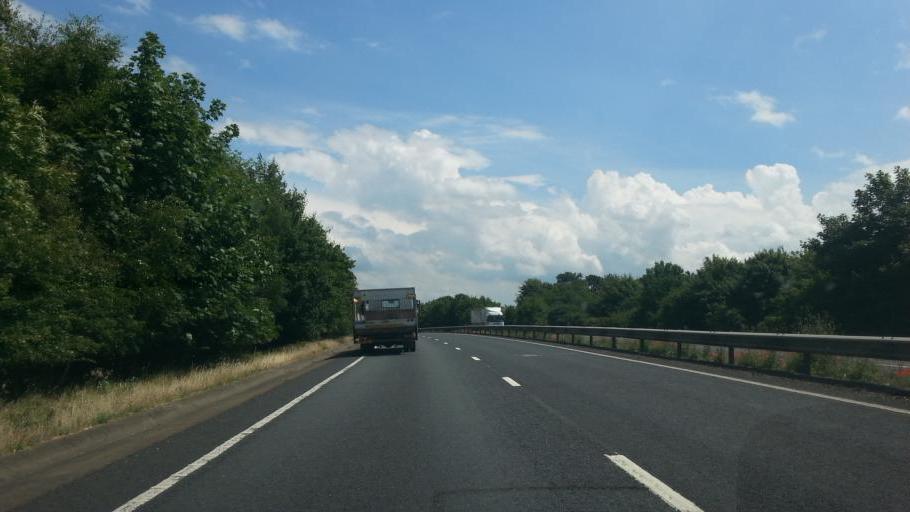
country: GB
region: England
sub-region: Norfolk
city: Thetford
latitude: 52.4324
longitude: 0.7700
